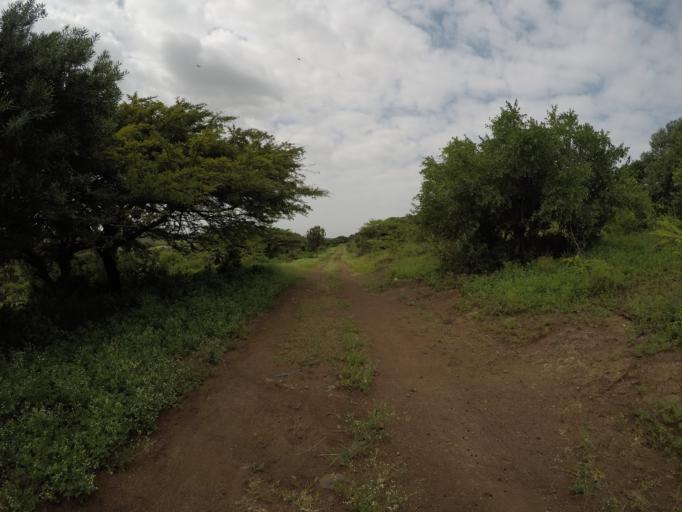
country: ZA
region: KwaZulu-Natal
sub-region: uThungulu District Municipality
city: Empangeni
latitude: -28.6272
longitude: 31.9098
